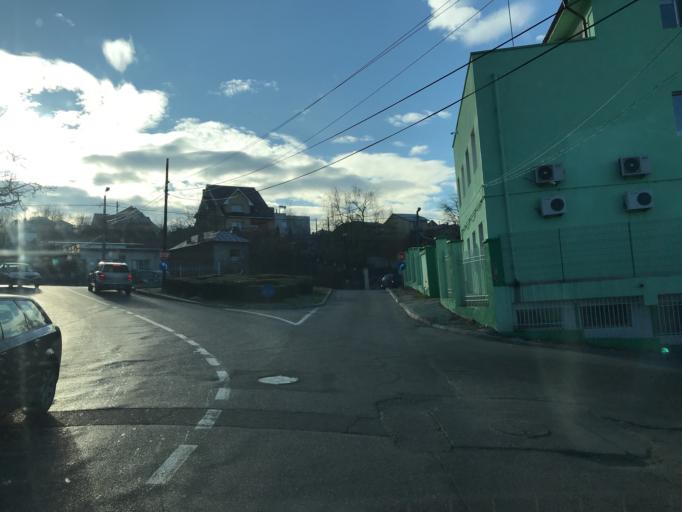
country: RO
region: Olt
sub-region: Municipiul Slatina
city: Slatina
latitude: 44.4285
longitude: 24.3609
